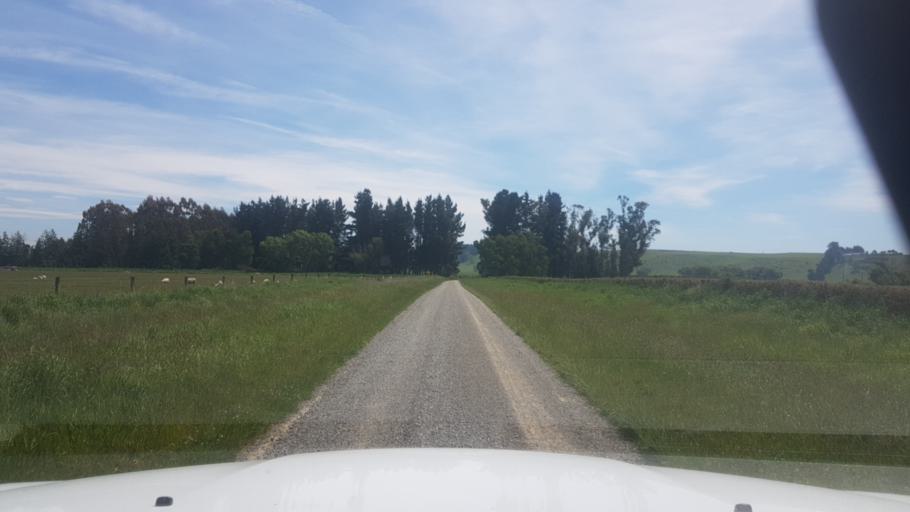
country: NZ
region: Canterbury
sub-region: Timaru District
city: Pleasant Point
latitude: -44.2224
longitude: 171.1633
